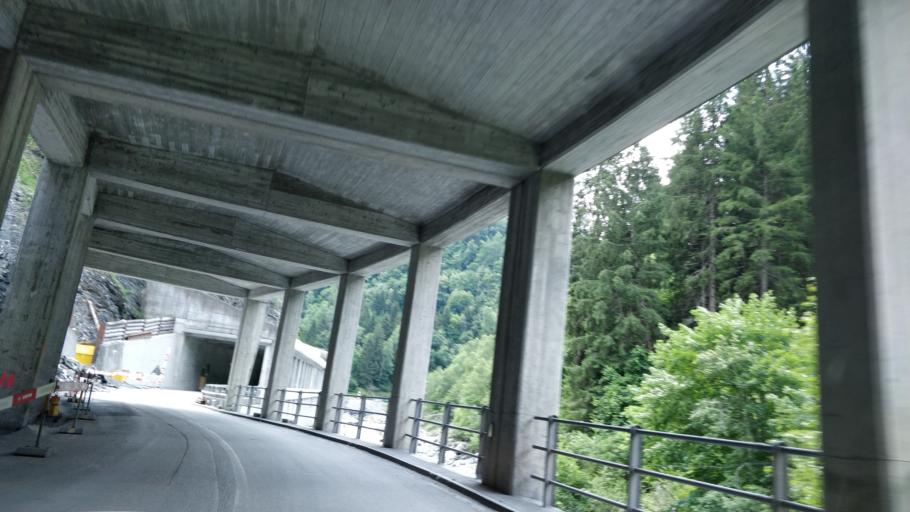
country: CH
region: Grisons
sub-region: Surselva District
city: Ilanz
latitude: 46.7420
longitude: 9.2178
